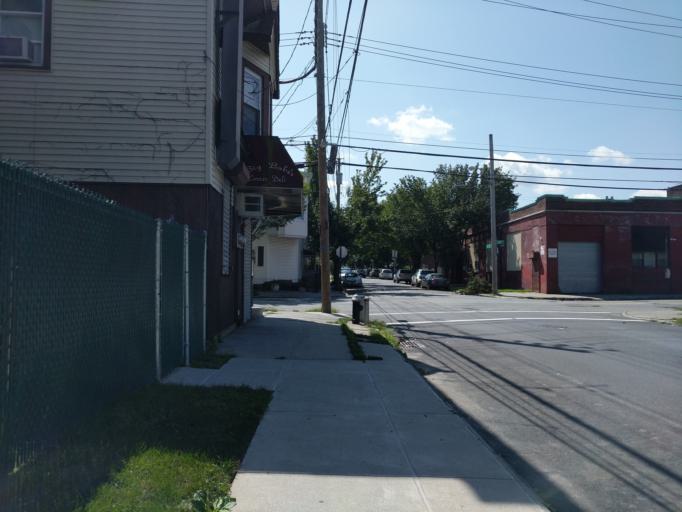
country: US
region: New Jersey
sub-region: Hudson County
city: Bayonne
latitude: 40.6323
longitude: -74.1228
